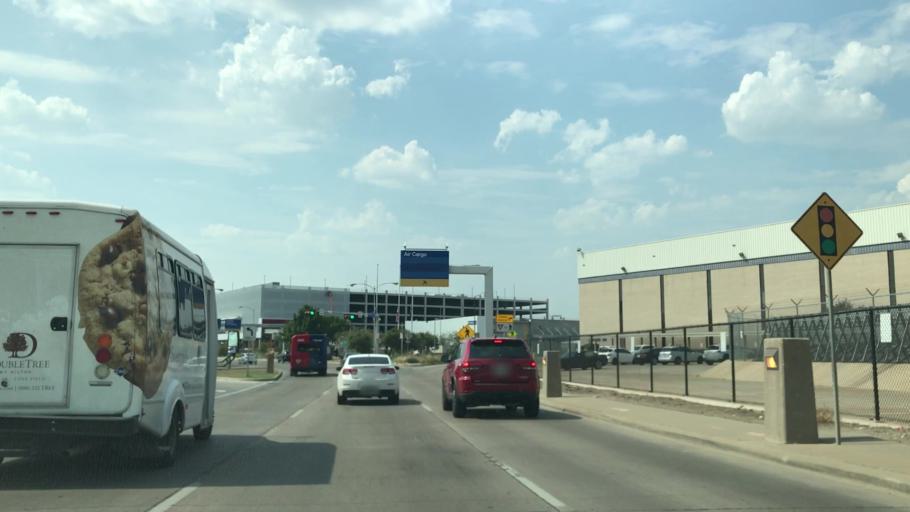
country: US
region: Texas
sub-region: Dallas County
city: University Park
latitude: 32.8402
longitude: -96.8455
